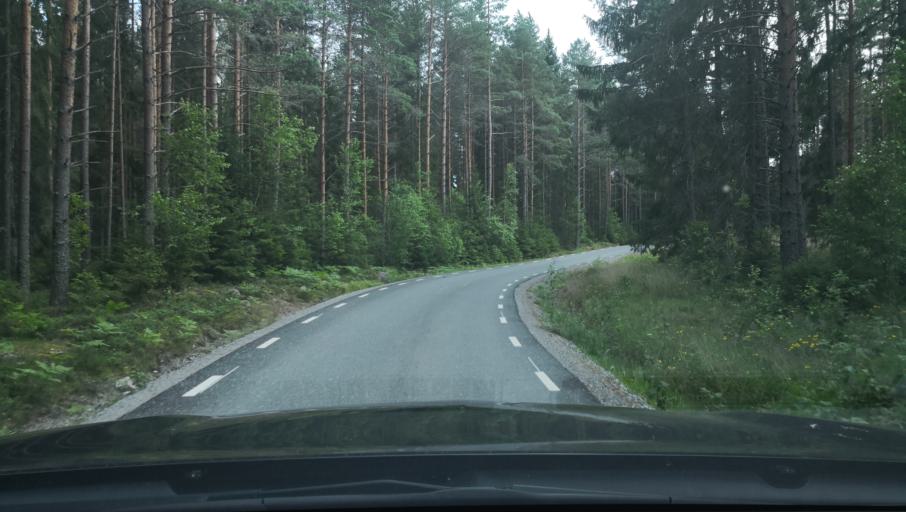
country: SE
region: Vaestmanland
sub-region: Surahammars Kommun
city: Surahammar
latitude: 59.6679
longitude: 16.1390
